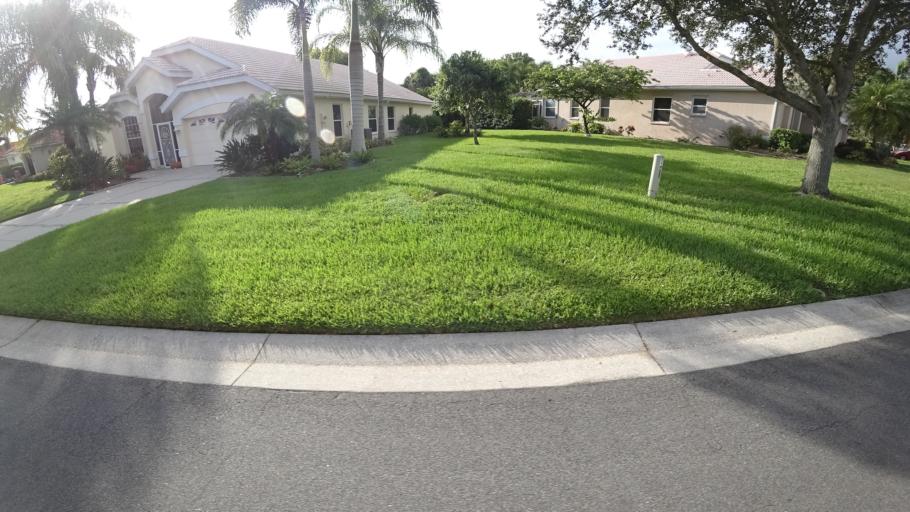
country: US
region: Florida
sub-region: Sarasota County
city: Desoto Lakes
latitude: 27.4225
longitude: -82.4859
